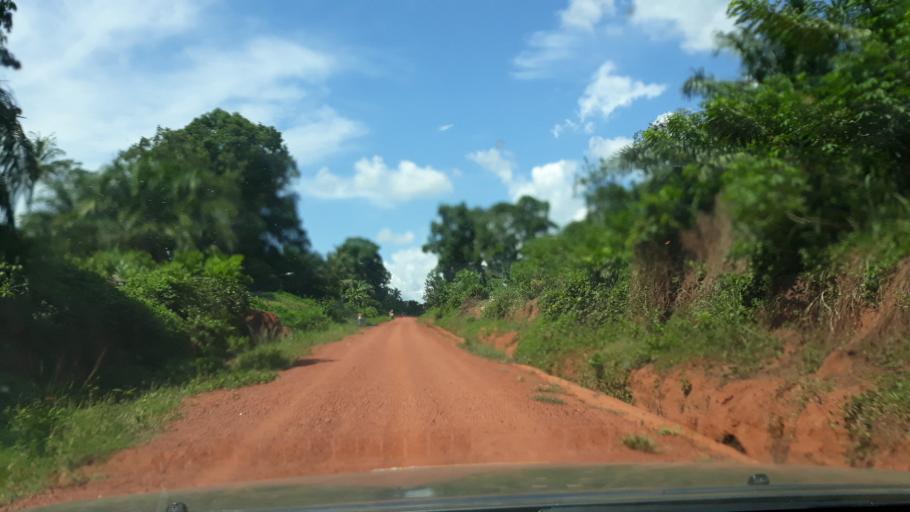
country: CD
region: Equateur
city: Businga
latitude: 3.4078
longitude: 20.3959
